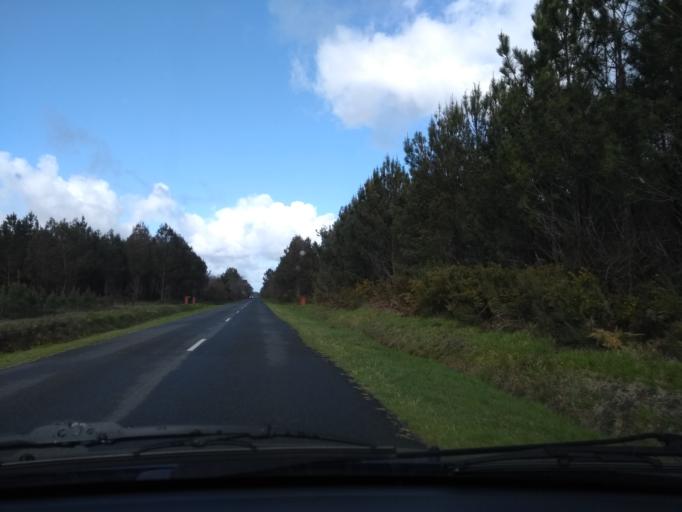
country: FR
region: Aquitaine
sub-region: Departement de la Gironde
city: Mios
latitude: 44.5509
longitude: -0.9503
